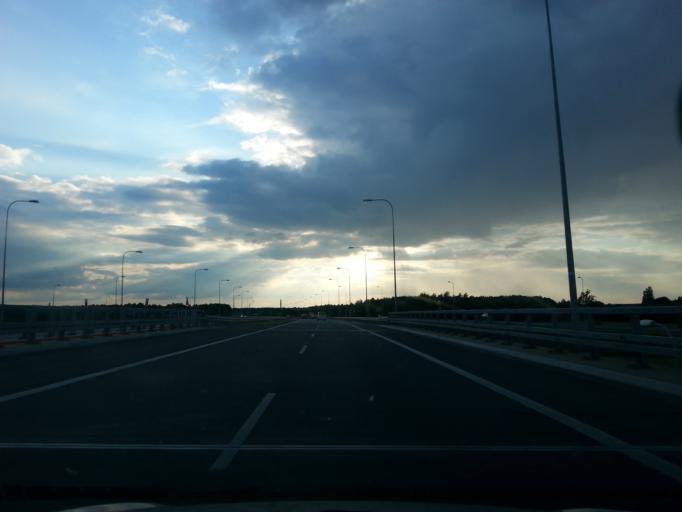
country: PL
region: Lodz Voivodeship
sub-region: Powiat zdunskowolski
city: Zapolice
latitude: 51.5974
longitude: 18.8748
